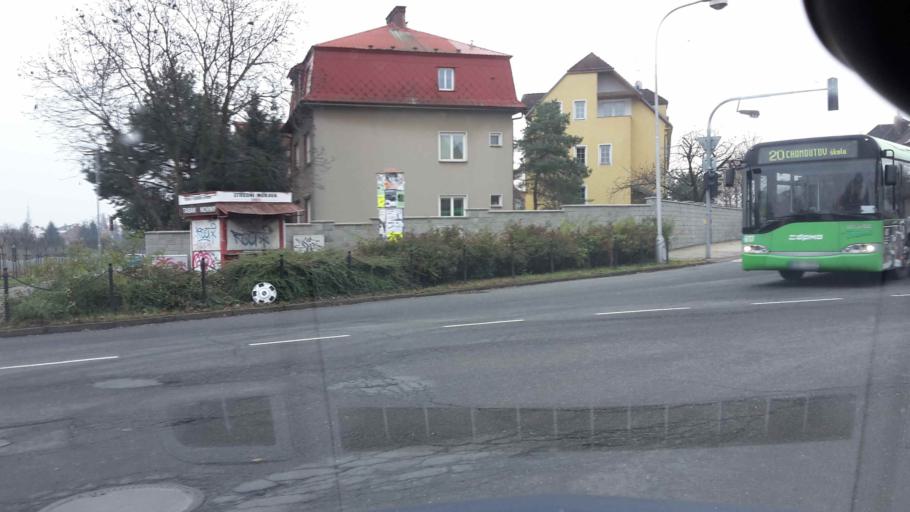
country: CZ
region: Olomoucky
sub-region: Okres Olomouc
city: Olomouc
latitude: 49.6020
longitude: 17.2368
